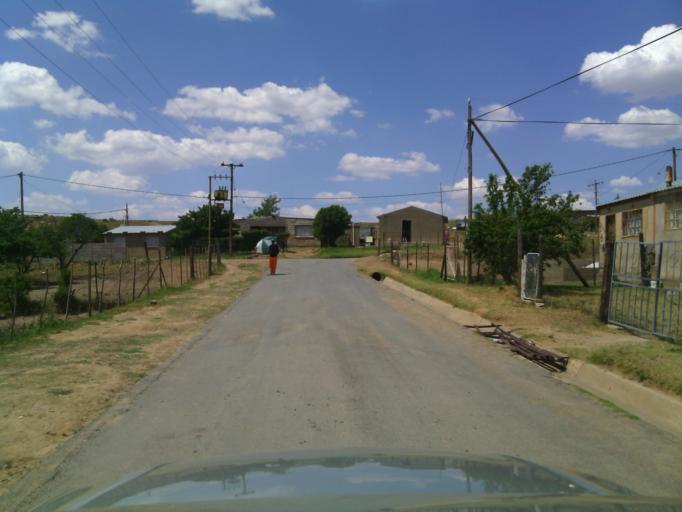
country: ZA
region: Orange Free State
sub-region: Xhariep District Municipality
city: Dewetsdorp
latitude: -29.5857
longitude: 26.6801
